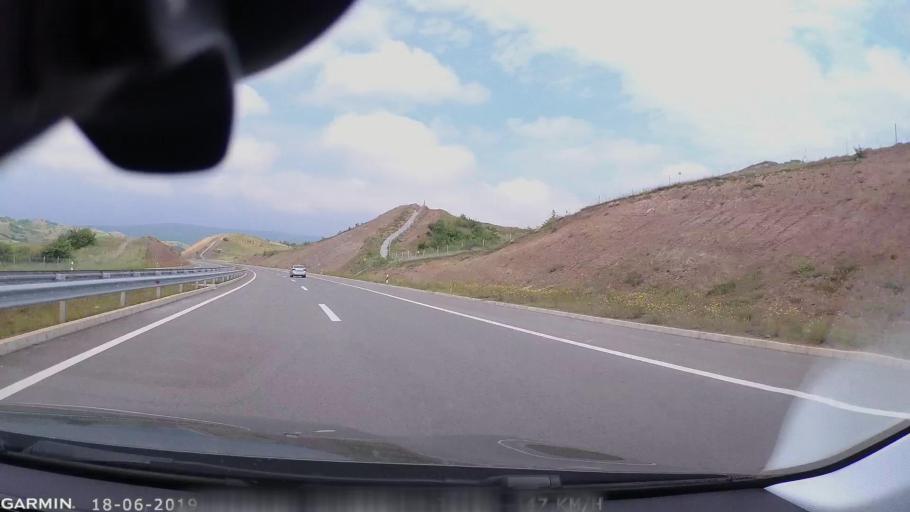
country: MK
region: Sveti Nikole
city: Gorobinci
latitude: 41.9263
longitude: 21.8346
